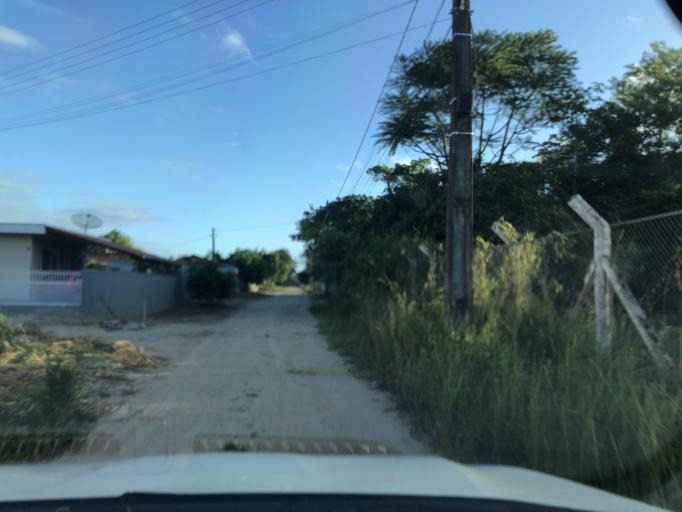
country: BR
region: Santa Catarina
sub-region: Sao Francisco Do Sul
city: Sao Francisco do Sul
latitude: -26.2274
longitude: -48.5263
